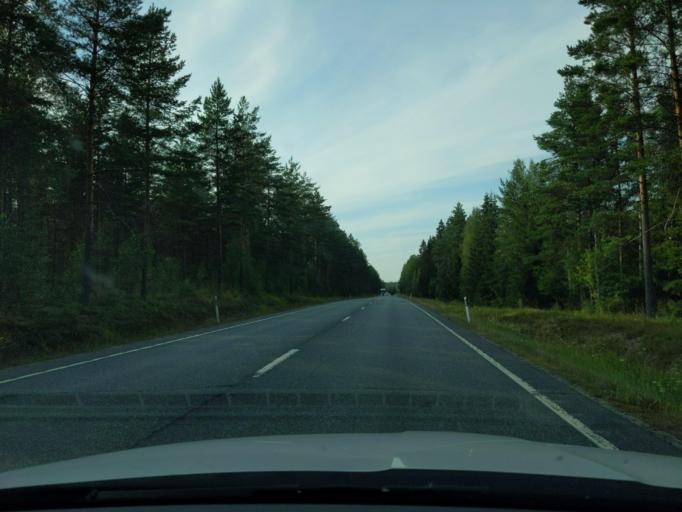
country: FI
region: Paijanne Tavastia
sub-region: Lahti
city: Padasjoki
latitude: 61.2918
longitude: 25.3091
